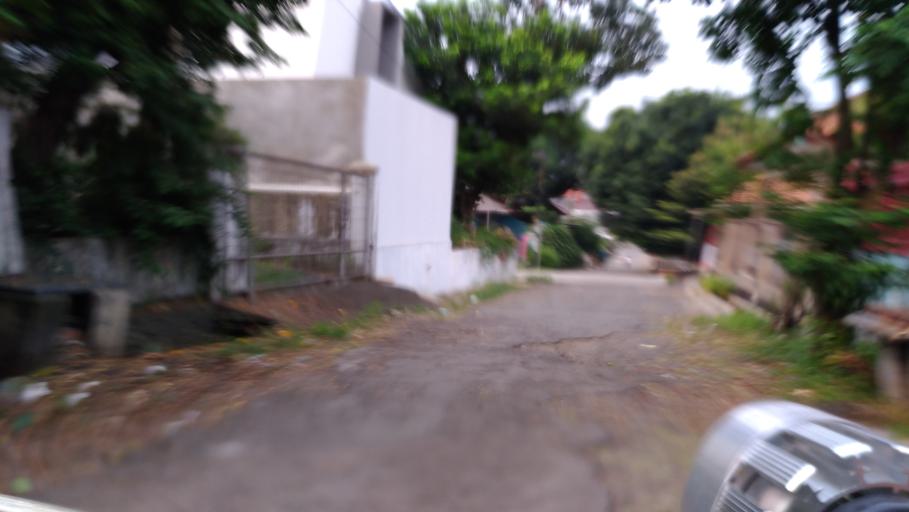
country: ID
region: West Java
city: Depok
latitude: -6.3635
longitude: 106.8635
